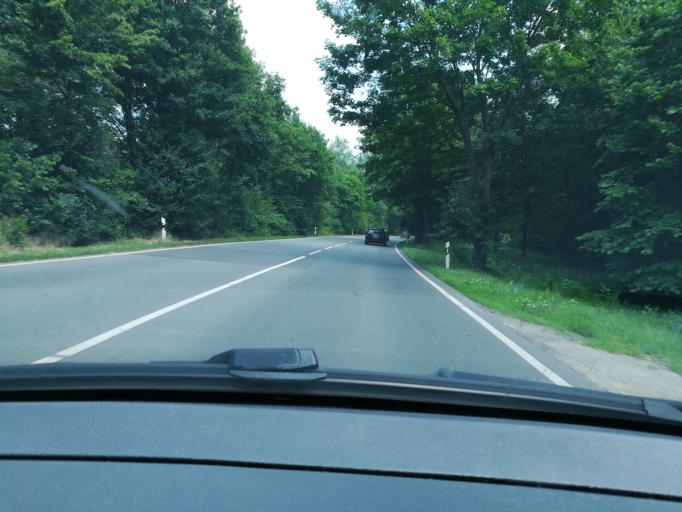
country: DE
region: North Rhine-Westphalia
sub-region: Regierungsbezirk Detmold
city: Minden
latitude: 52.3097
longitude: 8.9669
